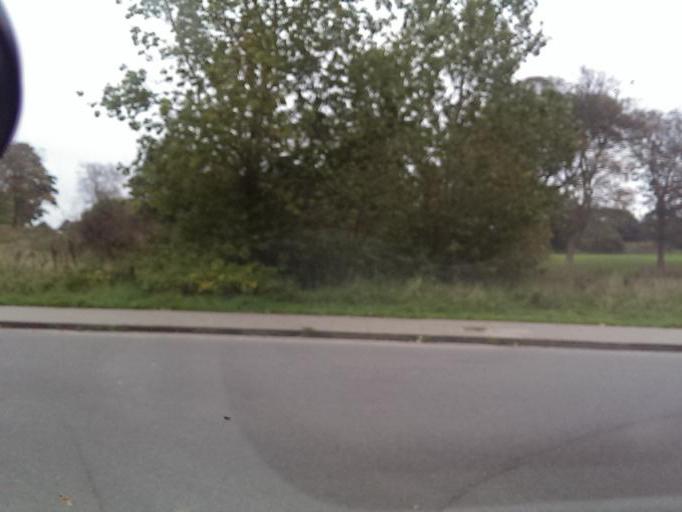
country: DK
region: South Denmark
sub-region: Esbjerg Kommune
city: Esbjerg
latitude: 55.4899
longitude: 8.4480
